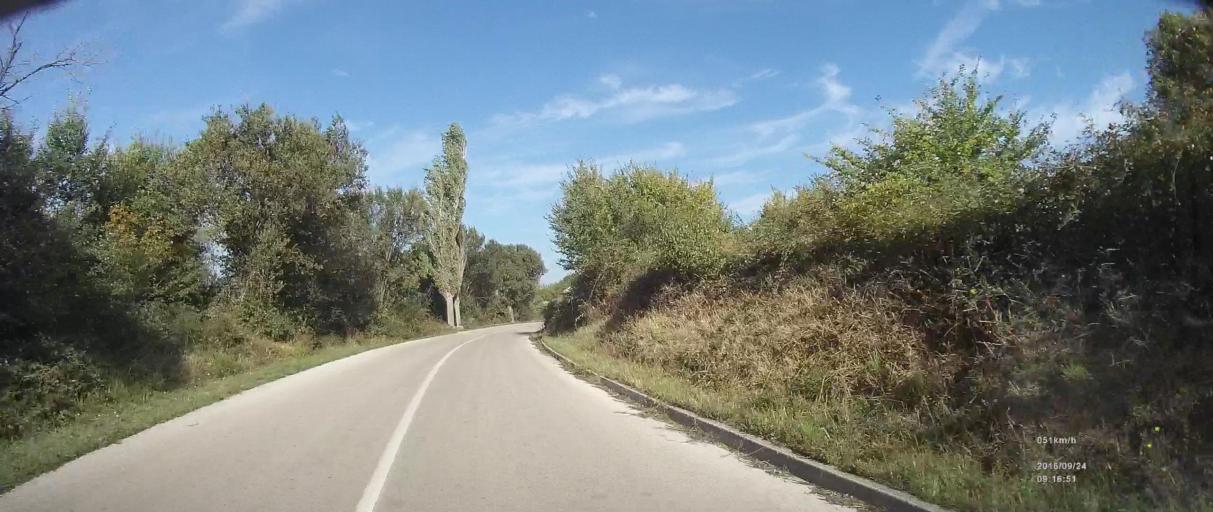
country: HR
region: Zadarska
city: Polaca
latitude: 44.0488
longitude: 15.5259
